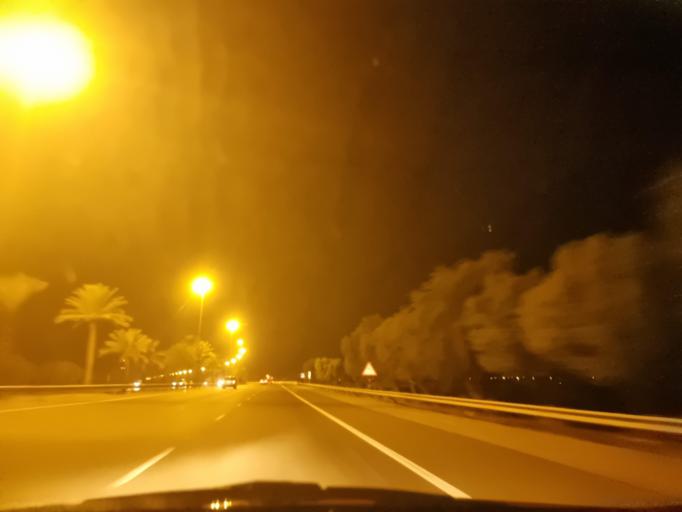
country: AE
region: Abu Dhabi
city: Al Ain
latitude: 24.2012
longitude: 55.3735
